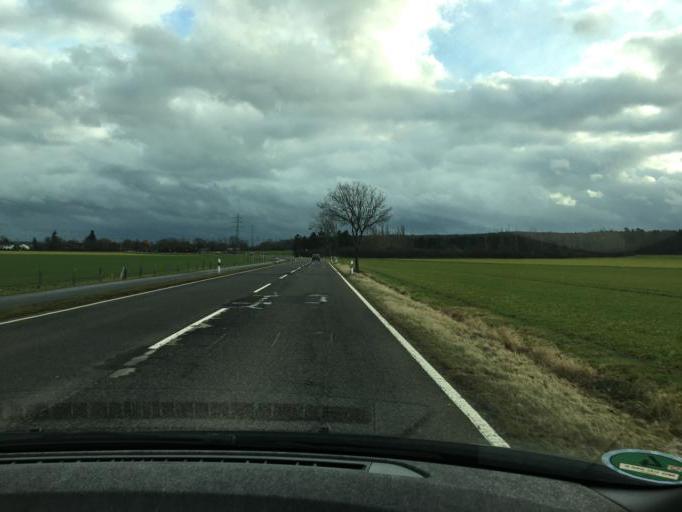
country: DE
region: North Rhine-Westphalia
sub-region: Regierungsbezirk Koln
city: Euskirchen
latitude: 50.6409
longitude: 6.7574
